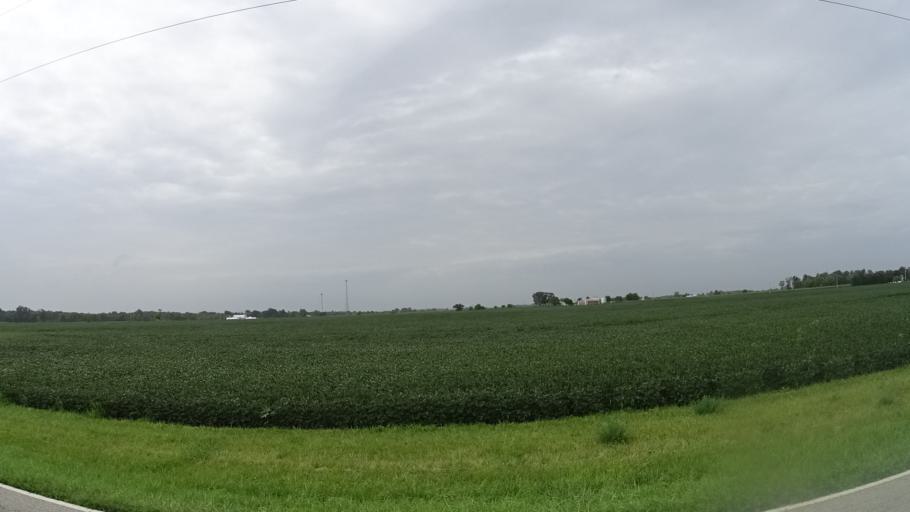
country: US
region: Indiana
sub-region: Madison County
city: Pendleton
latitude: 40.0298
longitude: -85.7864
